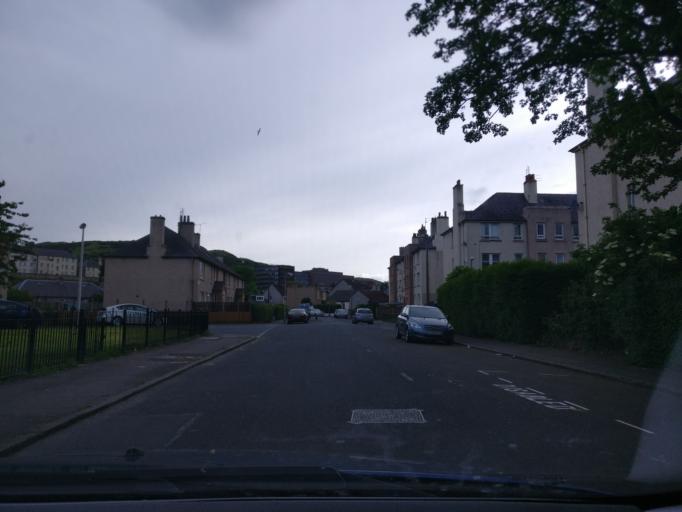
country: GB
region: Scotland
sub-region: West Lothian
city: Seafield
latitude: 55.9584
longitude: -3.1467
